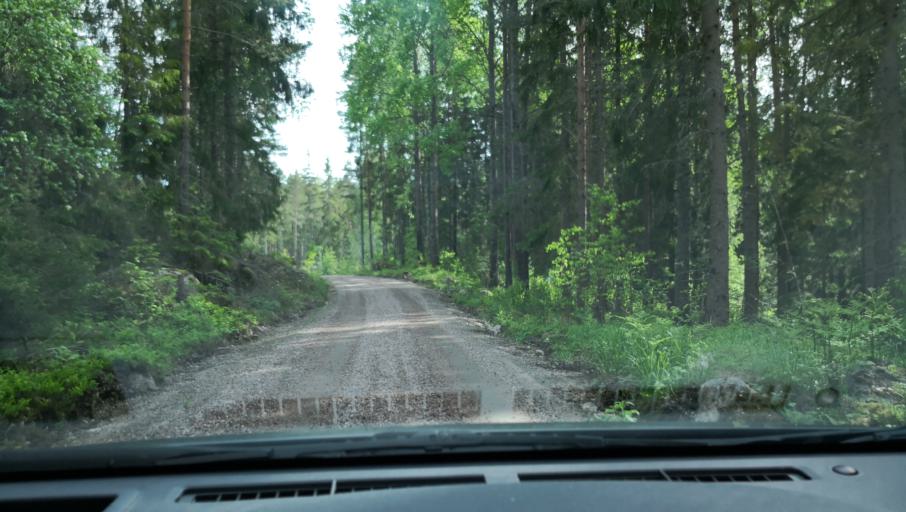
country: SE
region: Vaestmanland
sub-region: Arboga Kommun
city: Tyringe
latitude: 59.3483
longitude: 15.9344
